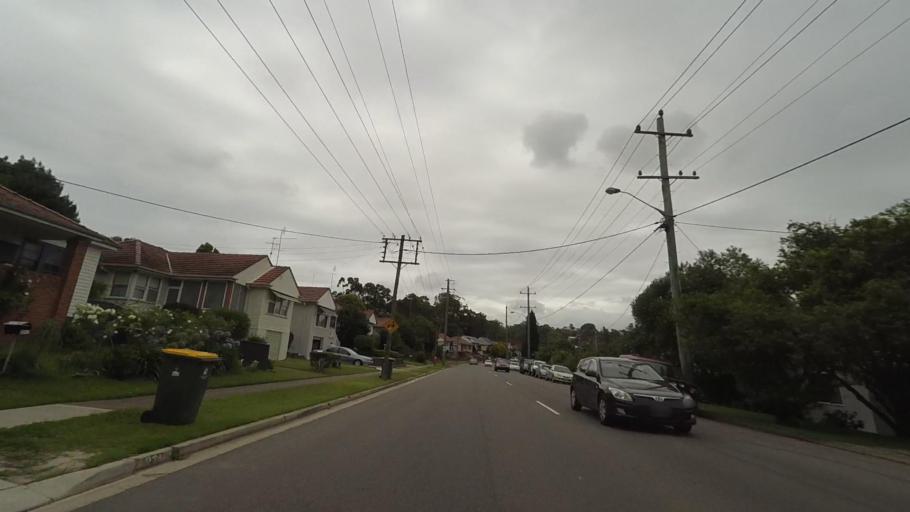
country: AU
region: New South Wales
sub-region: Lake Macquarie Shire
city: Kotara
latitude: -32.9448
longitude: 151.6935
